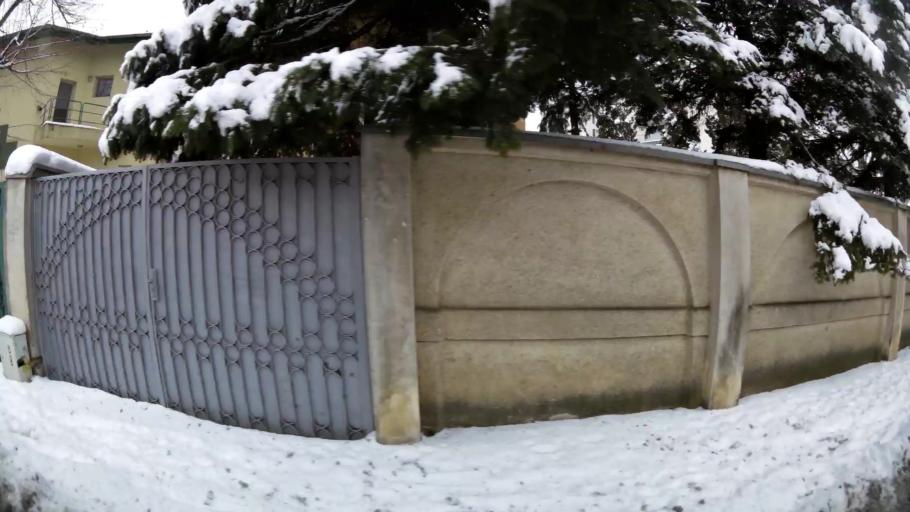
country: RO
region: Ilfov
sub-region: Comuna Otopeni
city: Otopeni
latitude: 44.5140
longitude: 26.1041
